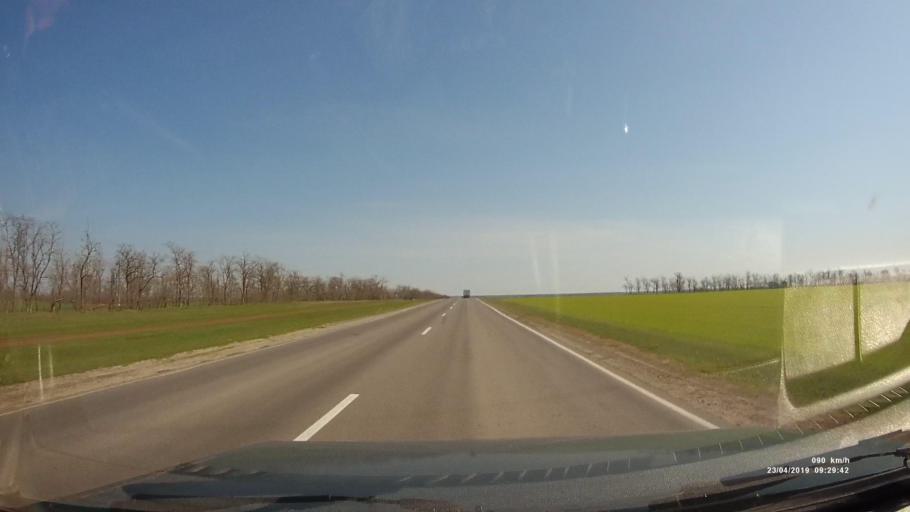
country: RU
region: Rostov
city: Gundorovskiy
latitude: 46.7632
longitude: 41.8077
